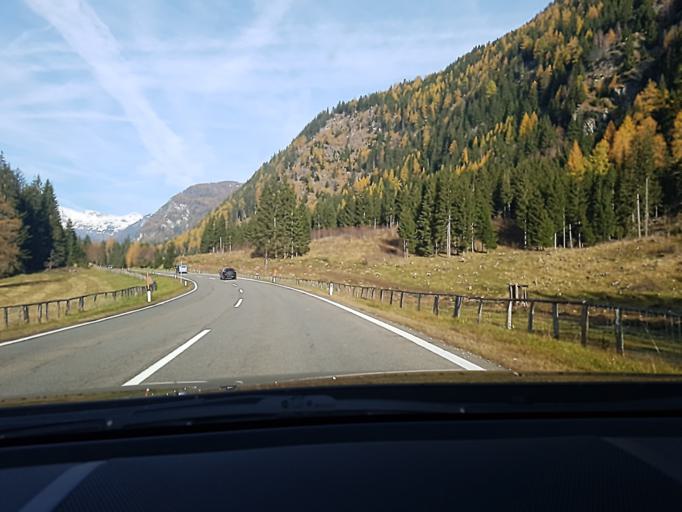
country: AT
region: Salzburg
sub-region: Politischer Bezirk Tamsweg
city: Mauterndorf
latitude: 47.1656
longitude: 13.6481
